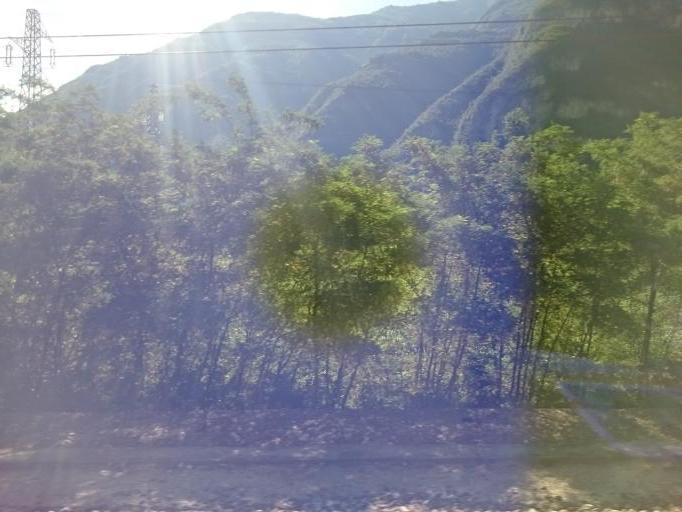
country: IT
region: Trentino-Alto Adige
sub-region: Provincia di Trento
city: Ala
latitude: 45.7493
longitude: 10.9880
